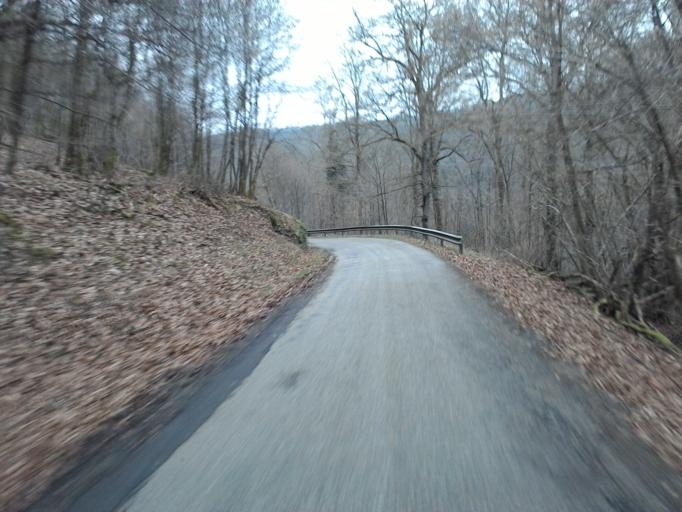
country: FR
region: Champagne-Ardenne
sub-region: Departement des Ardennes
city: Fromelennes
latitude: 50.0378
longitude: 4.8515
